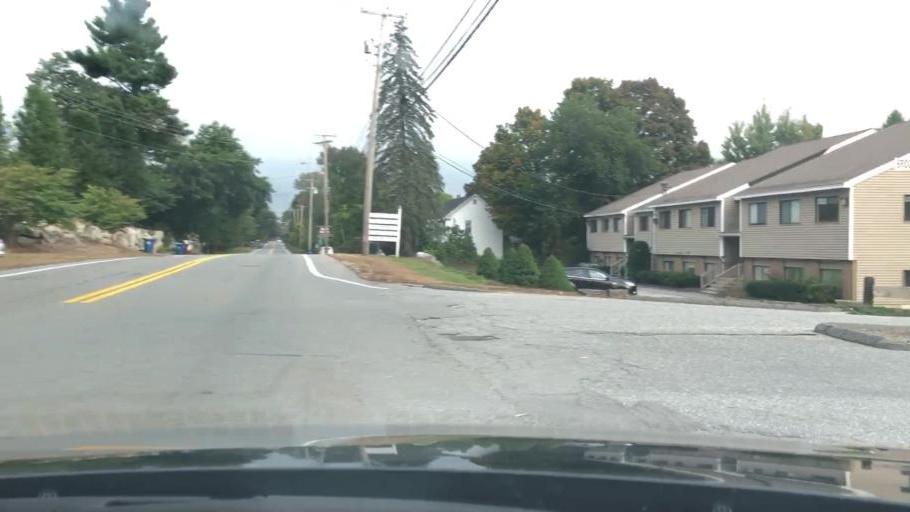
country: US
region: Massachusetts
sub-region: Middlesex County
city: Tyngsboro
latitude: 42.6585
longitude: -71.4044
